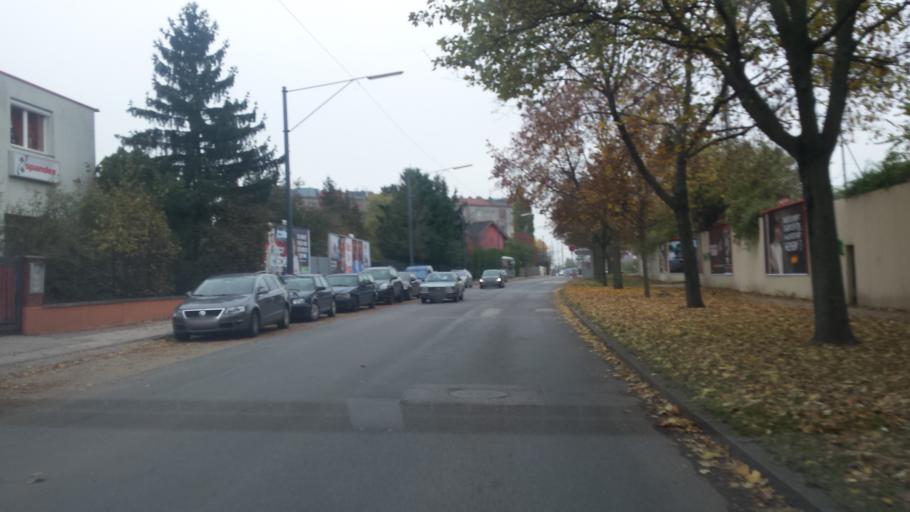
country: AT
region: Lower Austria
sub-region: Politischer Bezirk Wien-Umgebung
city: Schwechat
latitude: 48.1618
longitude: 16.4220
